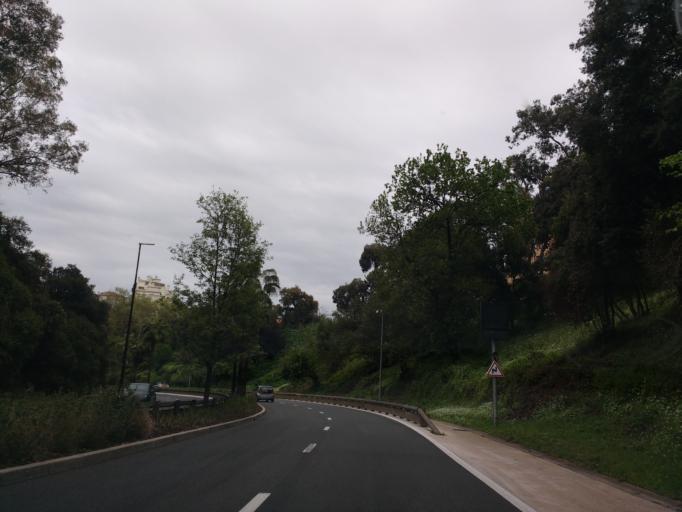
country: FR
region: Provence-Alpes-Cote d'Azur
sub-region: Departement des Alpes-Maritimes
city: Cannes
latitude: 43.5575
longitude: 7.0035
